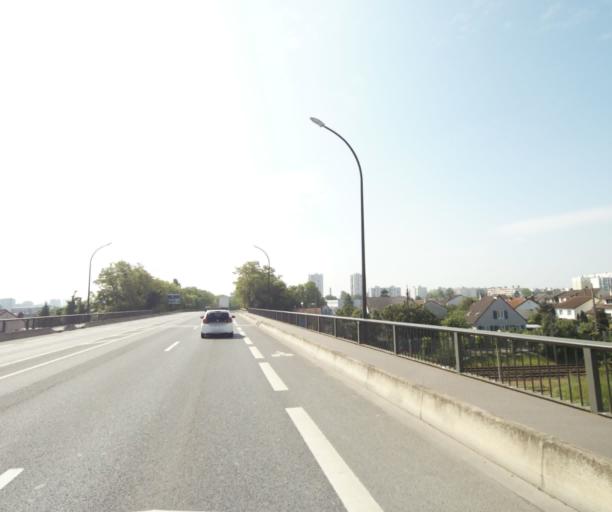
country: FR
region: Ile-de-France
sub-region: Departement du Val-d'Oise
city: Argenteuil
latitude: 48.9514
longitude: 2.2360
